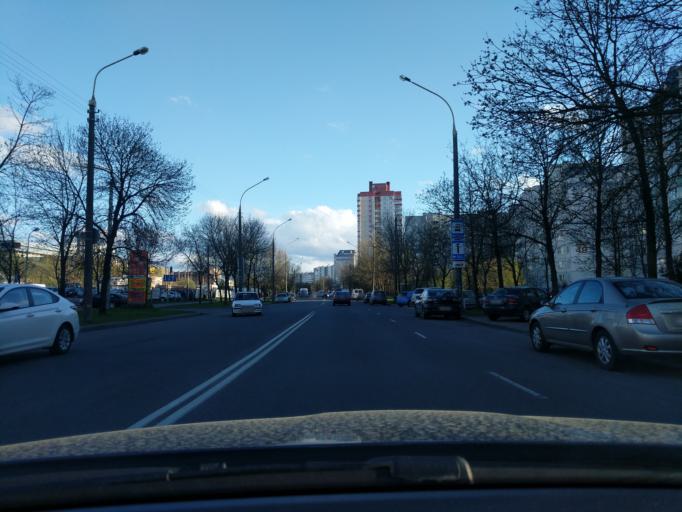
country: BY
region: Minsk
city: Novoye Medvezhino
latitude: 53.9165
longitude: 27.4495
